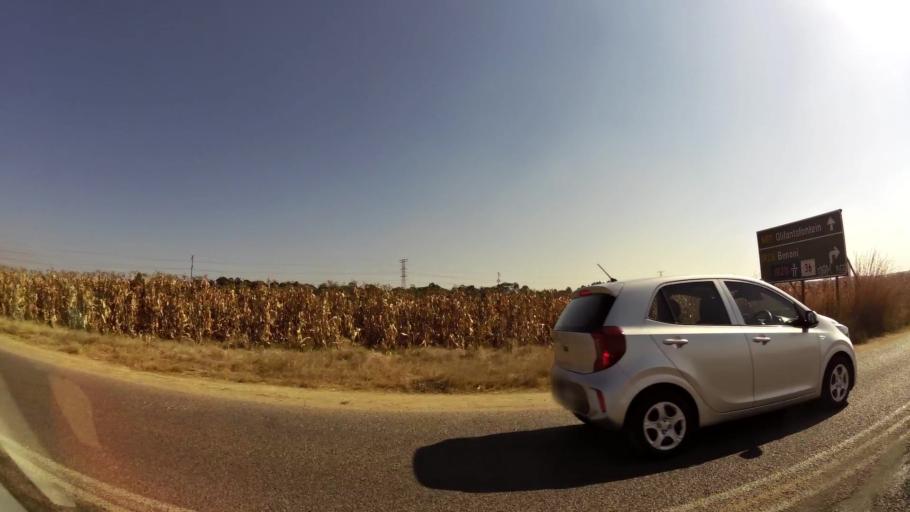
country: ZA
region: Gauteng
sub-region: Ekurhuleni Metropolitan Municipality
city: Tembisa
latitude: -26.0443
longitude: 28.2556
